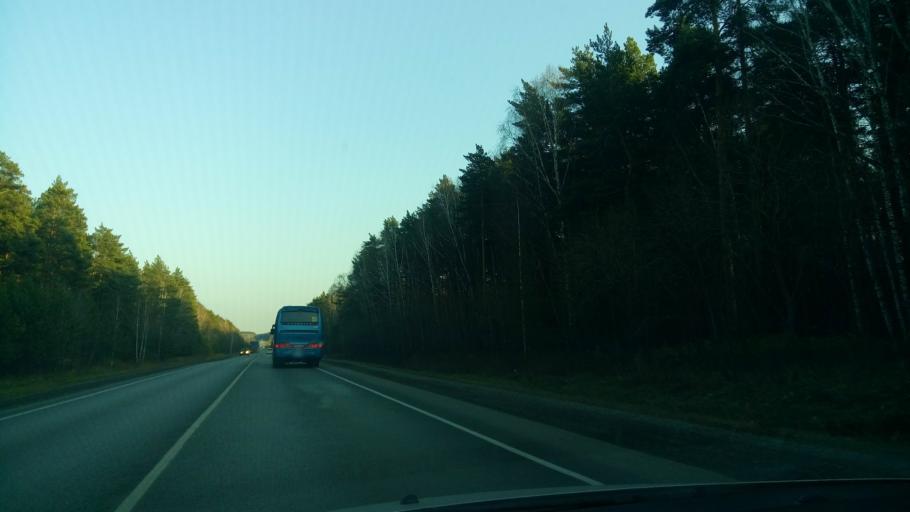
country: RU
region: Sverdlovsk
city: Gryaznovskoye
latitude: 56.7886
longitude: 61.7335
